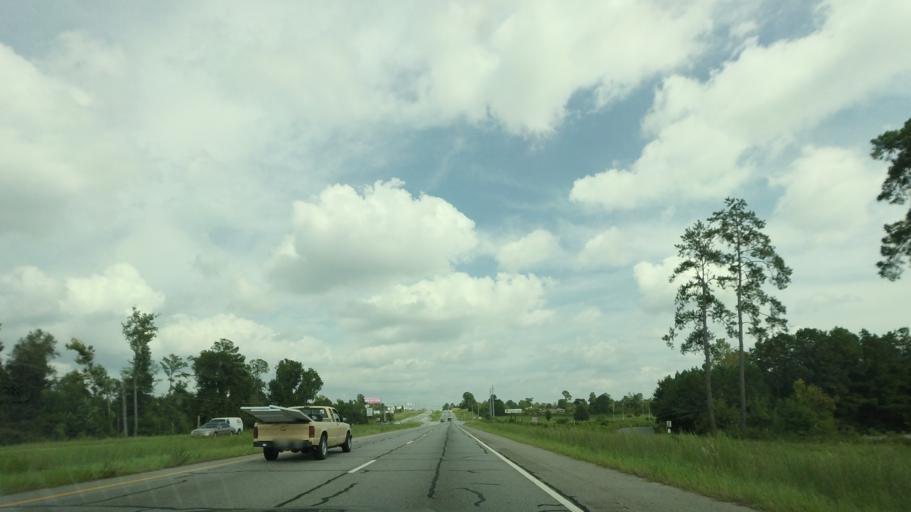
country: US
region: Georgia
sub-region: Bibb County
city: Macon
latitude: 32.8149
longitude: -83.6821
